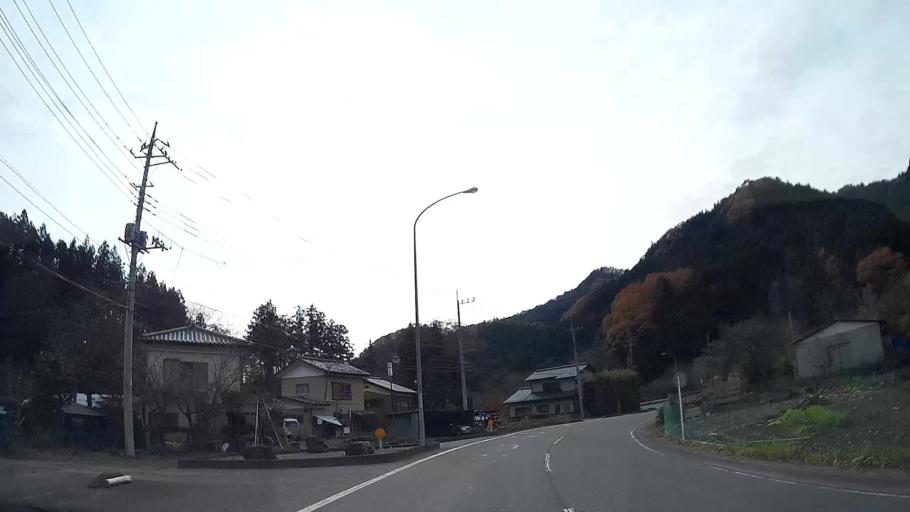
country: JP
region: Saitama
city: Chichibu
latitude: 36.0574
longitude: 138.9784
